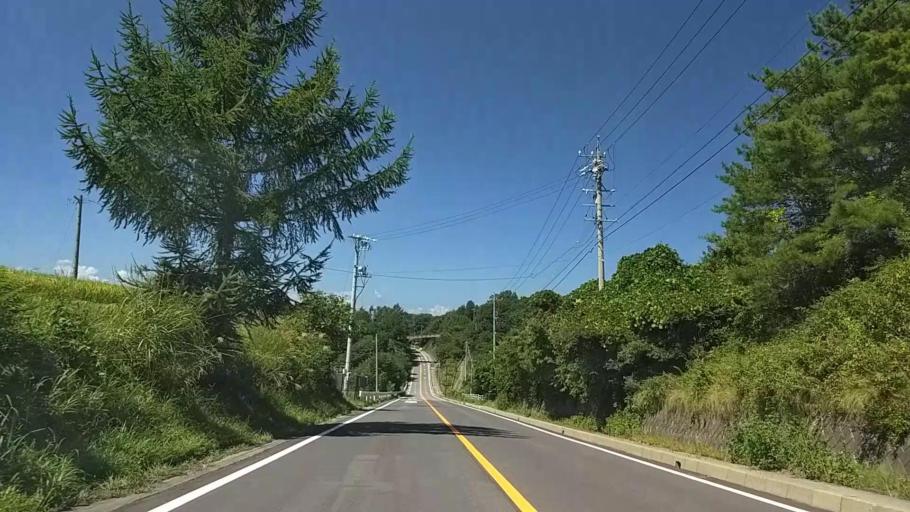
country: JP
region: Nagano
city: Komoro
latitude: 36.3511
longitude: 138.4158
